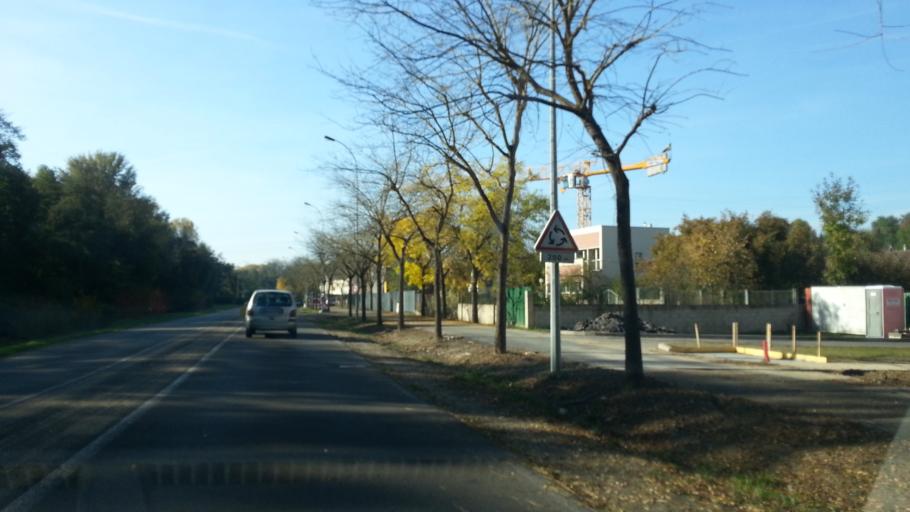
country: FR
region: Picardie
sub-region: Departement de l'Oise
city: Thiverny
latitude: 49.2559
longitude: 2.4241
